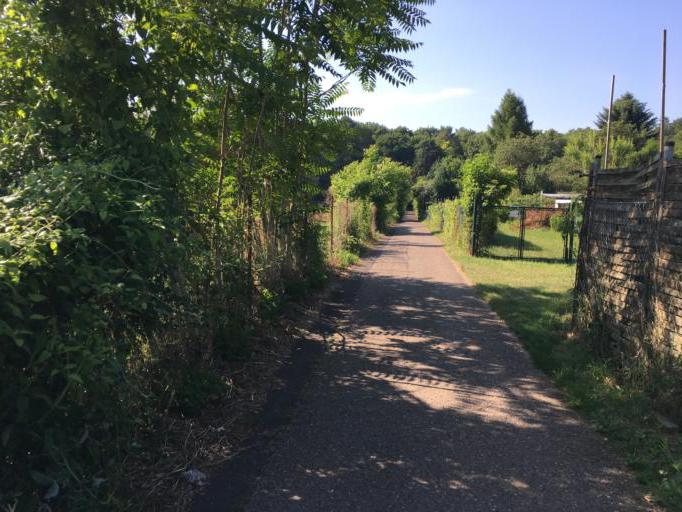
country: DE
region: Hesse
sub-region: Regierungsbezirk Darmstadt
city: Frankfurt am Main
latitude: 50.0915
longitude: 8.7194
